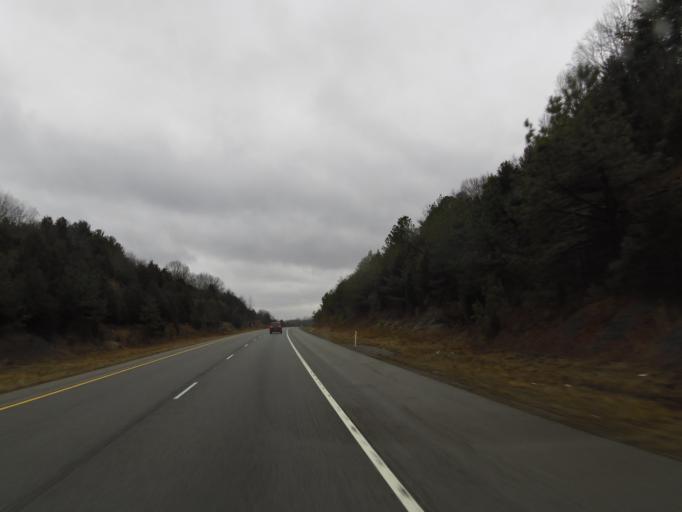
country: US
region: Illinois
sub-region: Johnson County
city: Vienna
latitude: 37.4977
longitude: -88.8978
